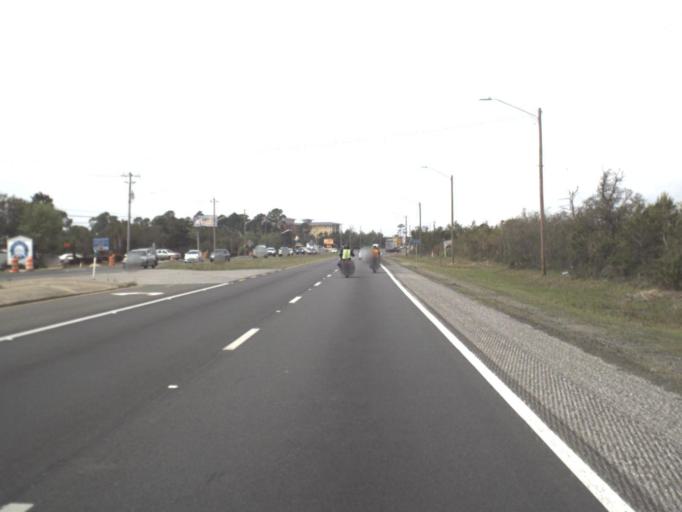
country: US
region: Florida
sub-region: Santa Rosa County
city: Navarre
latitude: 30.4048
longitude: -86.8519
